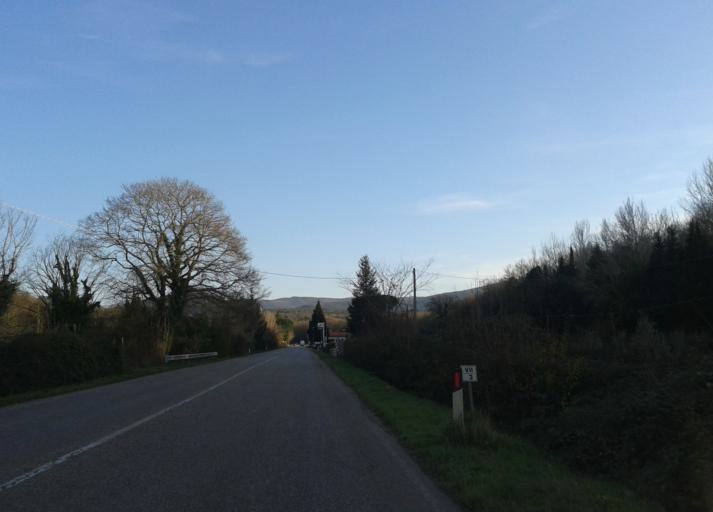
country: IT
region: Tuscany
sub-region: Provincia di Livorno
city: Guasticce
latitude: 43.5709
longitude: 10.3771
